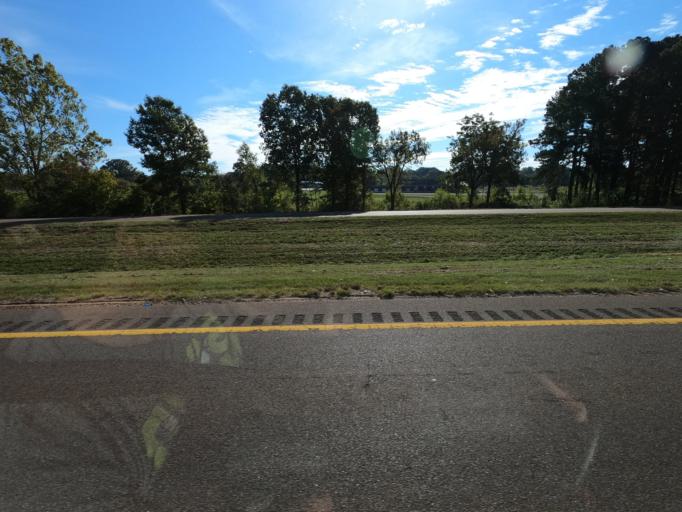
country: US
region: Tennessee
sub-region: Tipton County
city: Brighton
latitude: 35.4766
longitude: -89.7453
